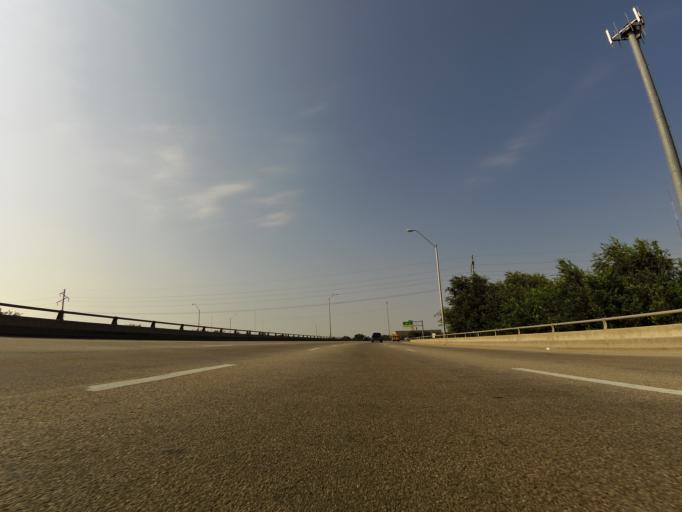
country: US
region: Kansas
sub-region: Sedgwick County
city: Wichita
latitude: 37.7146
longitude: -97.3217
